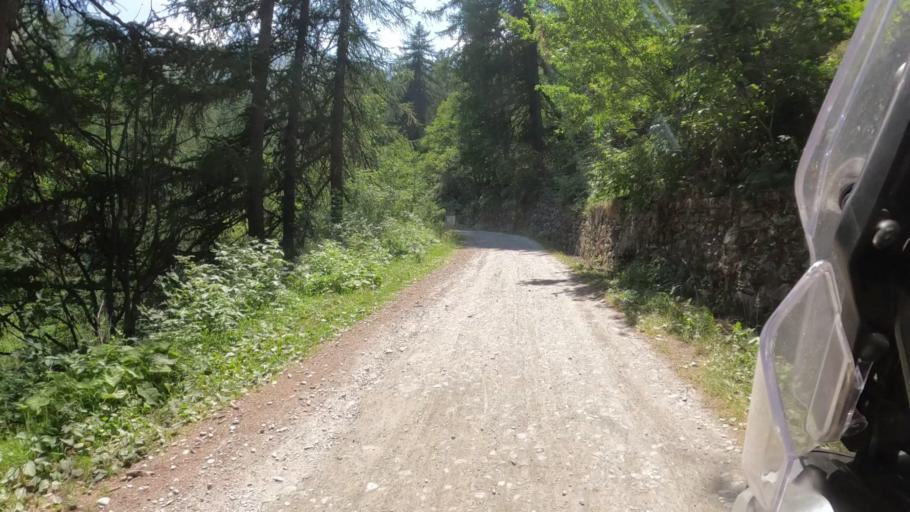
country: IT
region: Piedmont
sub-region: Provincia di Torino
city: Meana di Susa
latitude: 45.0917
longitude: 7.0601
